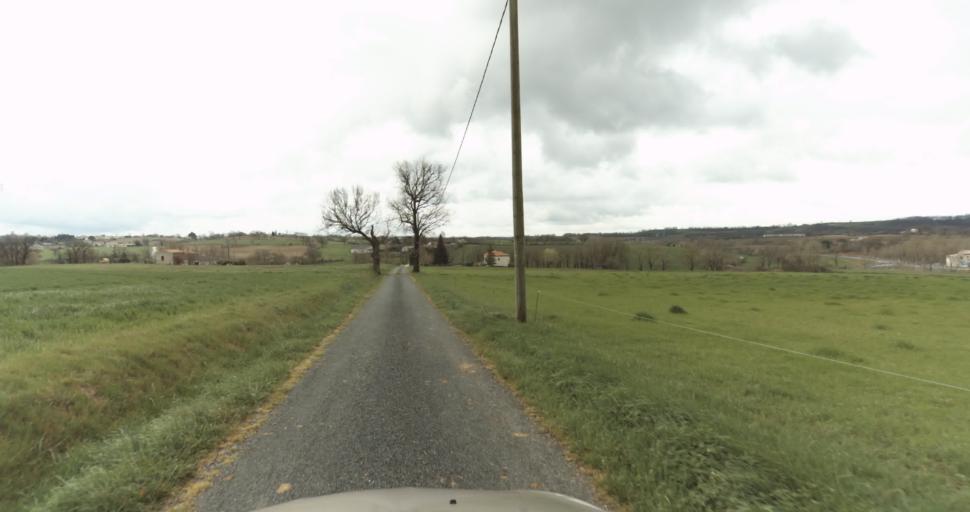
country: FR
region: Midi-Pyrenees
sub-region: Departement du Tarn
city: Frejairolles
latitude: 43.8589
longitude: 2.1937
